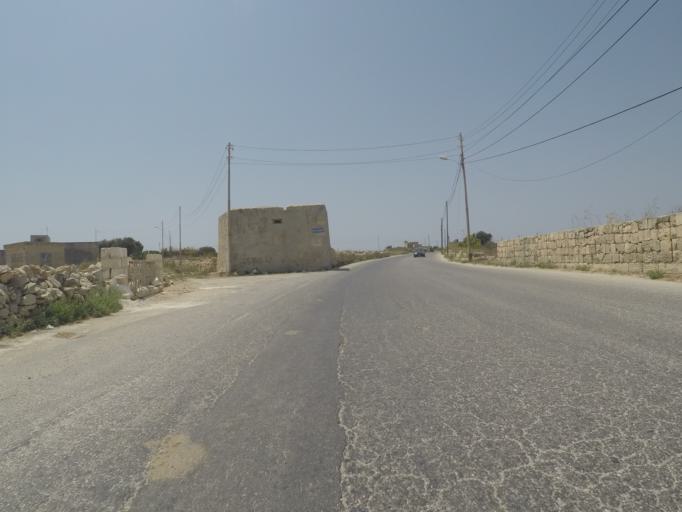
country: MT
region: Is-Siggiewi
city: Siggiewi
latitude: 35.8405
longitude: 14.4317
